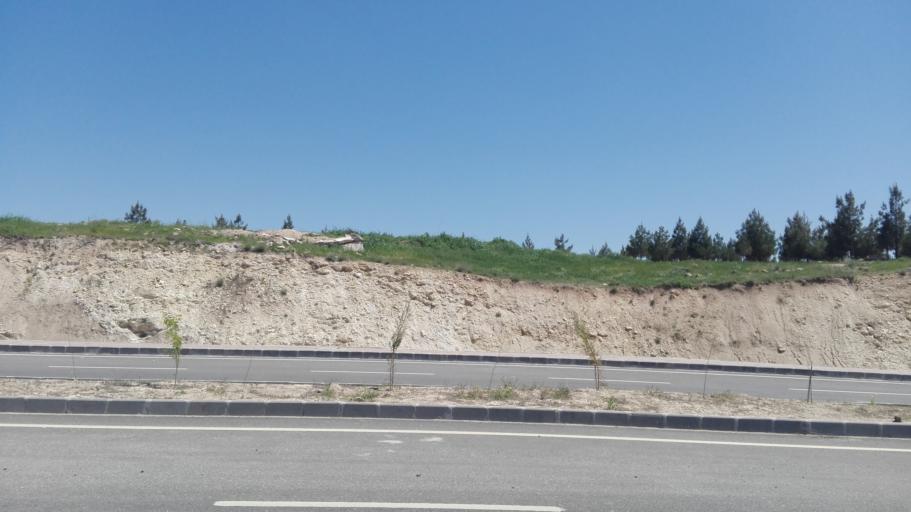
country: TR
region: Batman
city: Oymatas
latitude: 37.7837
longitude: 41.0624
